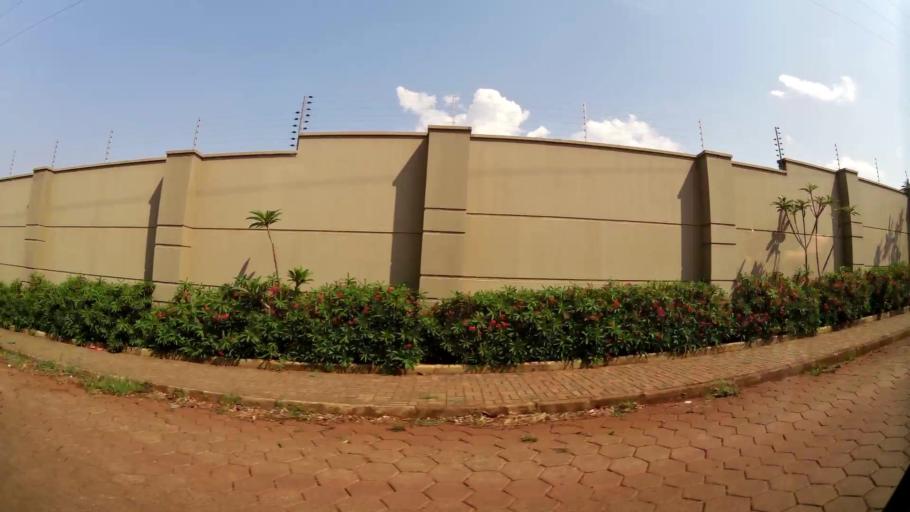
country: PY
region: Alto Parana
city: Ciudad del Este
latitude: -25.5132
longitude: -54.6238
